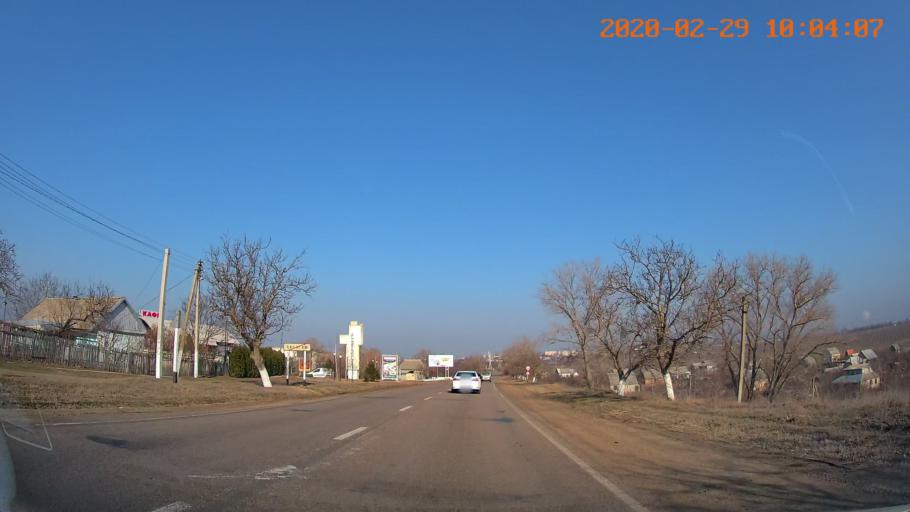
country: MD
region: Causeni
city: Chitcani
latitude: 46.7956
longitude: 29.6771
